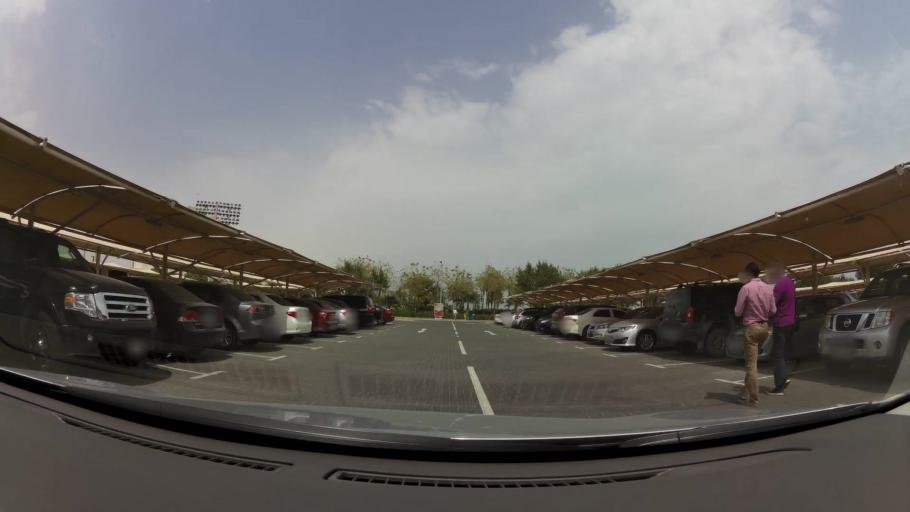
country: QA
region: Baladiyat ad Dawhah
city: Doha
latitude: 25.2931
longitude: 51.5409
